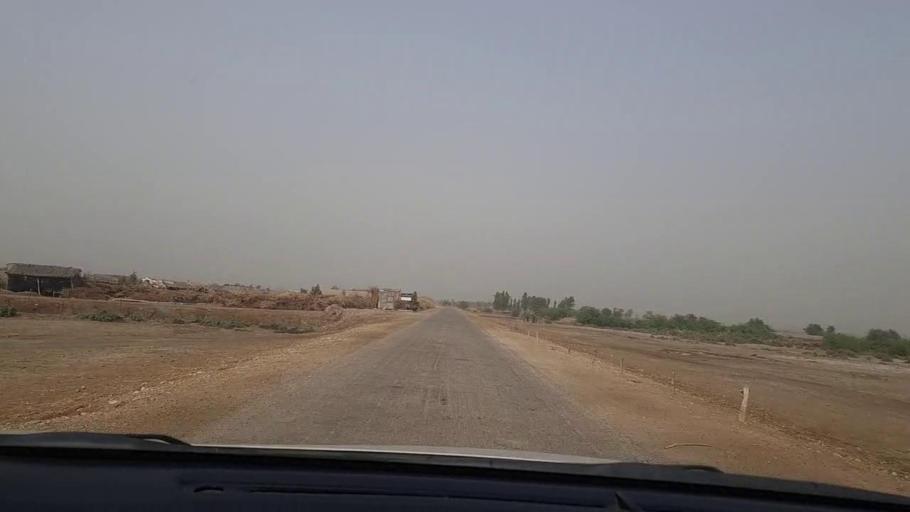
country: PK
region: Sindh
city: Samaro
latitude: 25.3856
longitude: 69.3637
